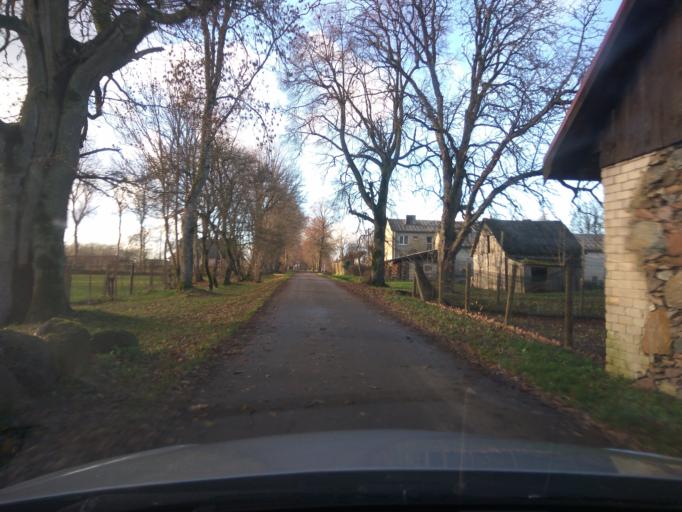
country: LV
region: Aizpute
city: Aizpute
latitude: 56.7497
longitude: 21.5831
